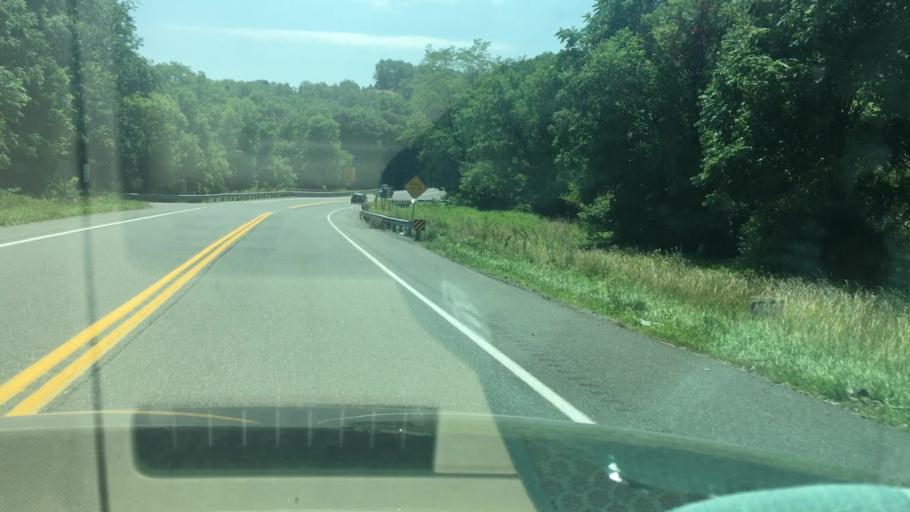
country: US
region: Pennsylvania
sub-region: Lehigh County
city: Schnecksville
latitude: 40.6586
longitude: -75.6854
